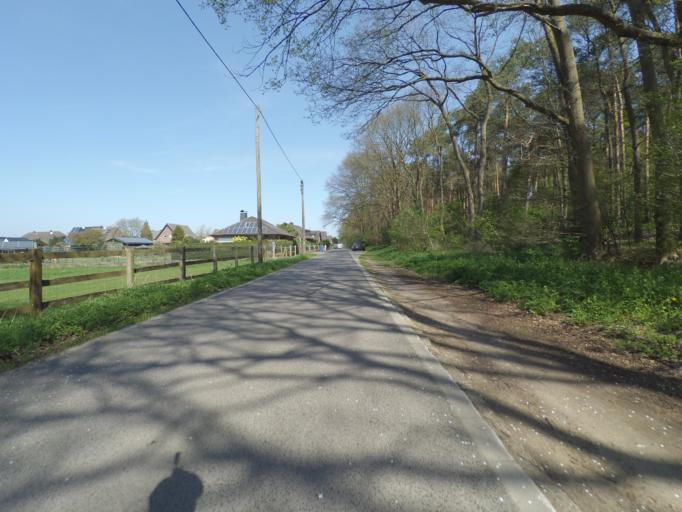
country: DE
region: North Rhine-Westphalia
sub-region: Regierungsbezirk Dusseldorf
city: Mehrhoog
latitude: 51.7353
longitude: 6.5330
